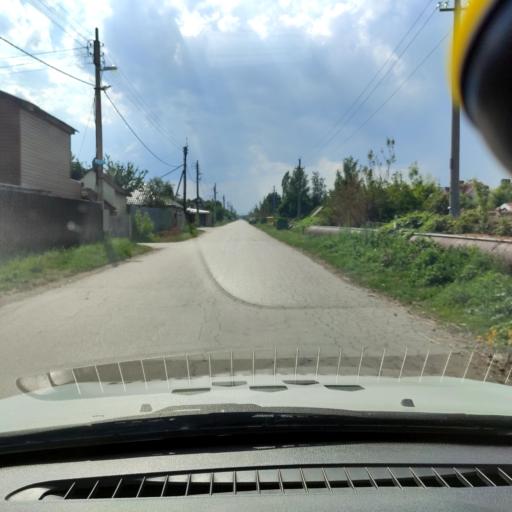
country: RU
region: Samara
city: Podstepki
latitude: 53.5074
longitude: 49.1471
